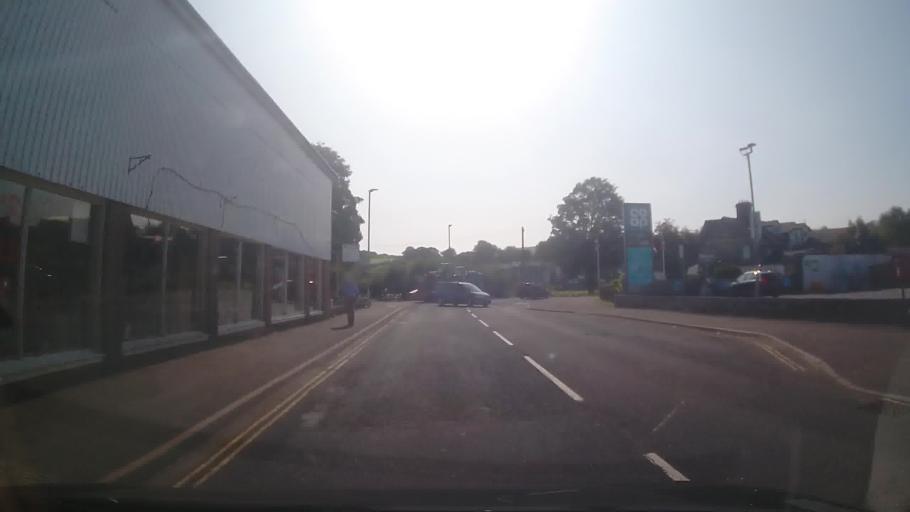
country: GB
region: Wales
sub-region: Sir Powys
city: Builth Wells
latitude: 52.1524
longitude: -3.4011
